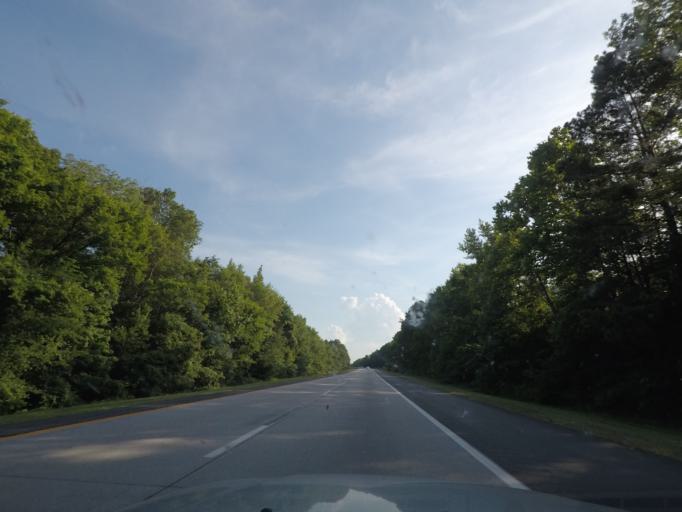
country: US
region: North Carolina
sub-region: Granville County
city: Creedmoor
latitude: 36.1837
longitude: -78.6944
